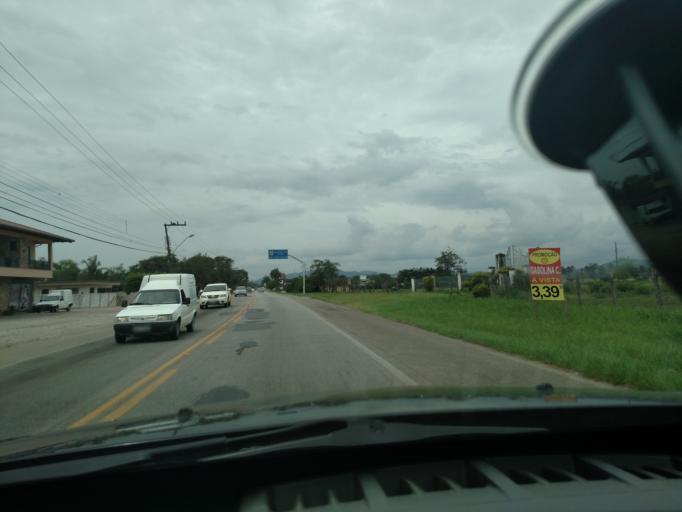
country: BR
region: Santa Catarina
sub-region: Gaspar
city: Gaspar
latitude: -26.9111
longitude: -48.9257
